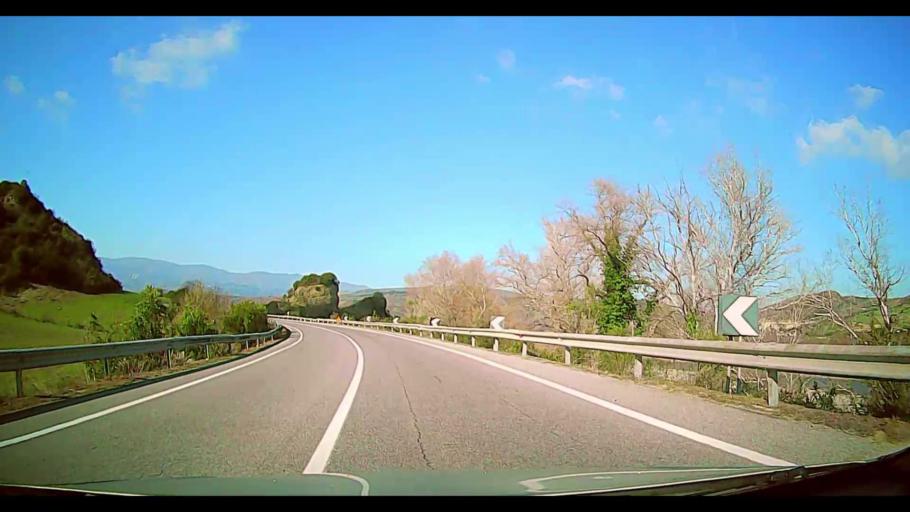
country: IT
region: Calabria
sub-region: Provincia di Crotone
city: Belvedere Spinello
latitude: 39.1913
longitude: 16.8819
